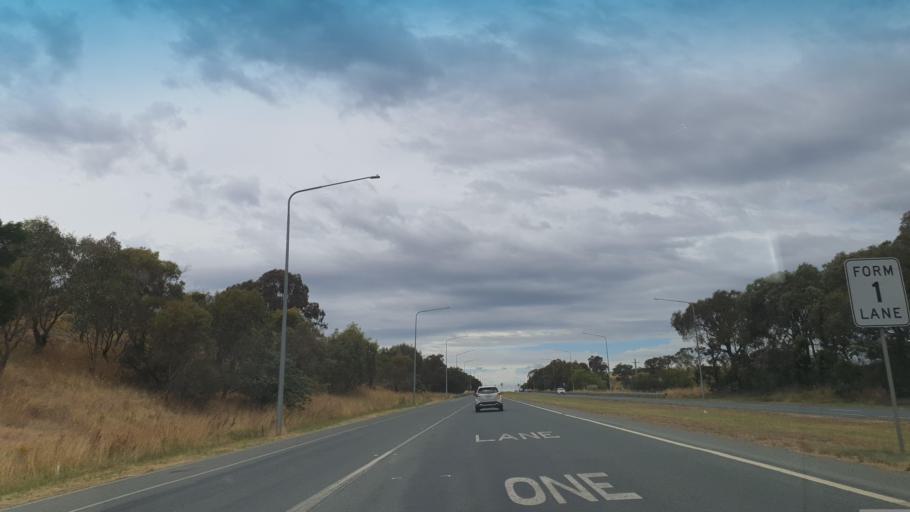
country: AU
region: Australian Capital Territory
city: Macquarie
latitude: -35.2707
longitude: 149.0552
